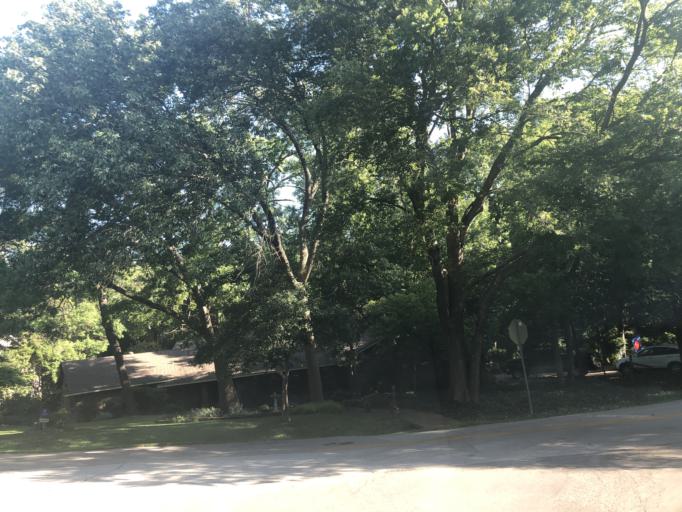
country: US
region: Texas
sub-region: Dallas County
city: Duncanville
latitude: 32.6734
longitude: -96.9180
